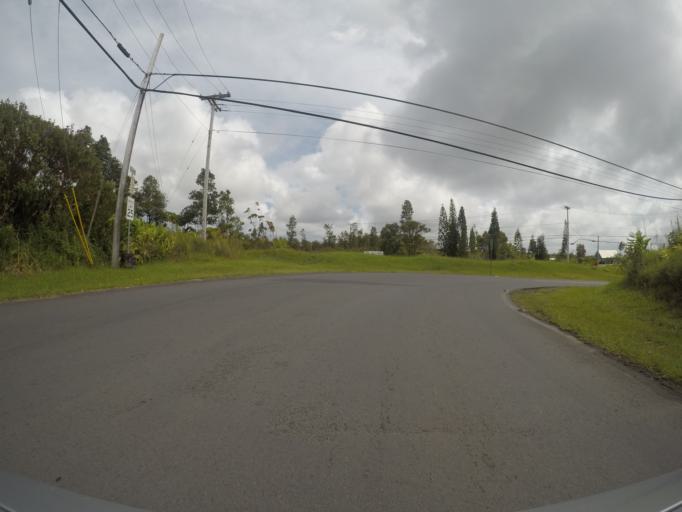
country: US
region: Hawaii
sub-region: Hawaii County
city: Fern Acres
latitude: 19.4787
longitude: -155.1423
